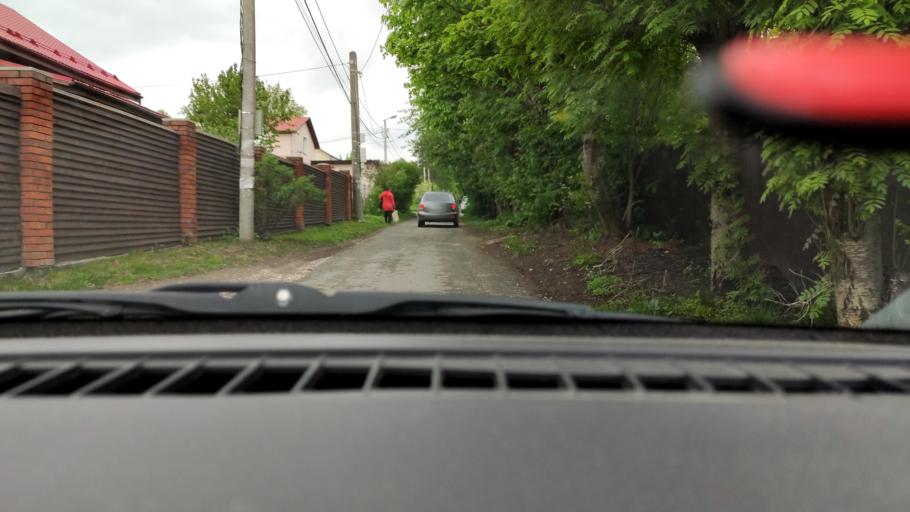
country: RU
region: Perm
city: Kondratovo
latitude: 58.0570
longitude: 56.1327
